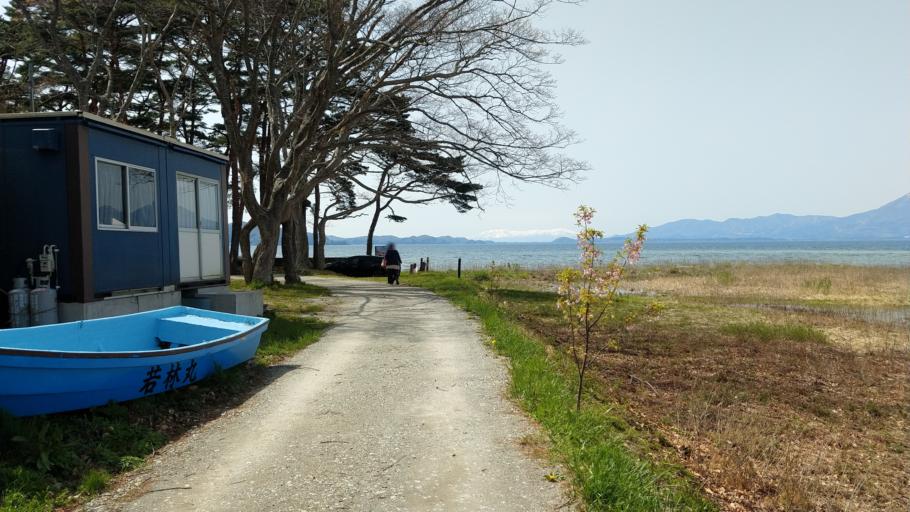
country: JP
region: Fukushima
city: Inawashiro
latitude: 37.4157
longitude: 140.1224
